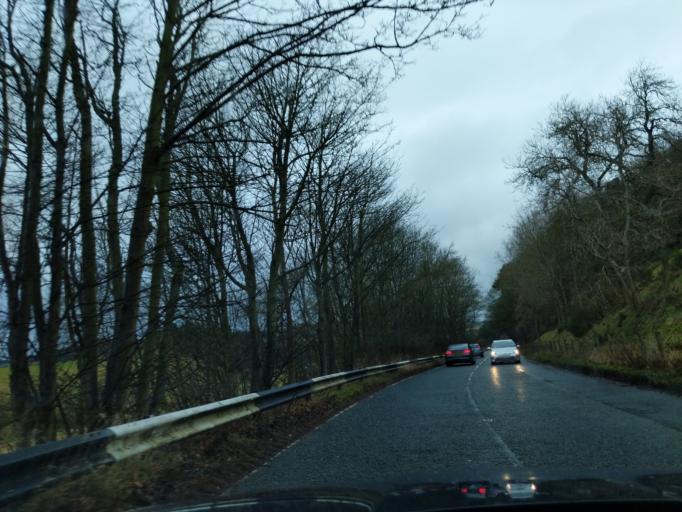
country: GB
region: Scotland
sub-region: The Scottish Borders
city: Galashiels
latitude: 55.6453
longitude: -2.8550
